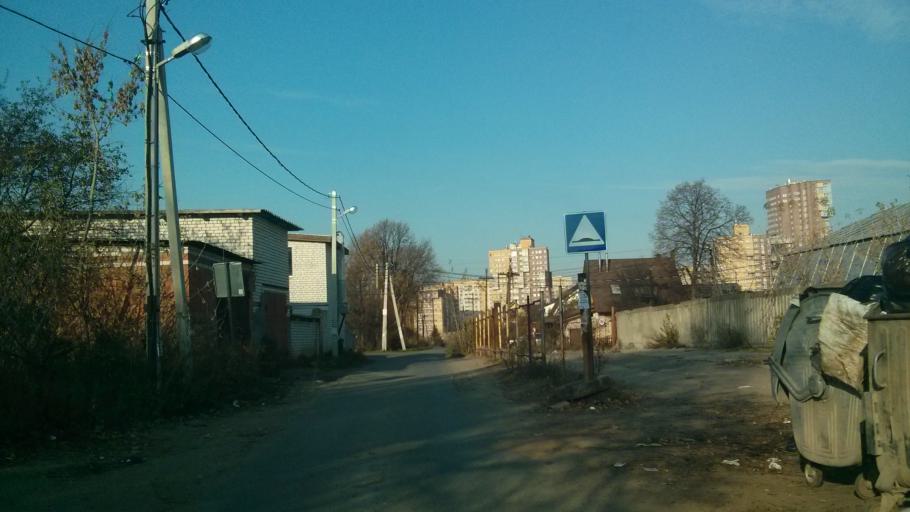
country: RU
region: Nizjnij Novgorod
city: Nizhniy Novgorod
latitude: 56.3034
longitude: 44.0329
